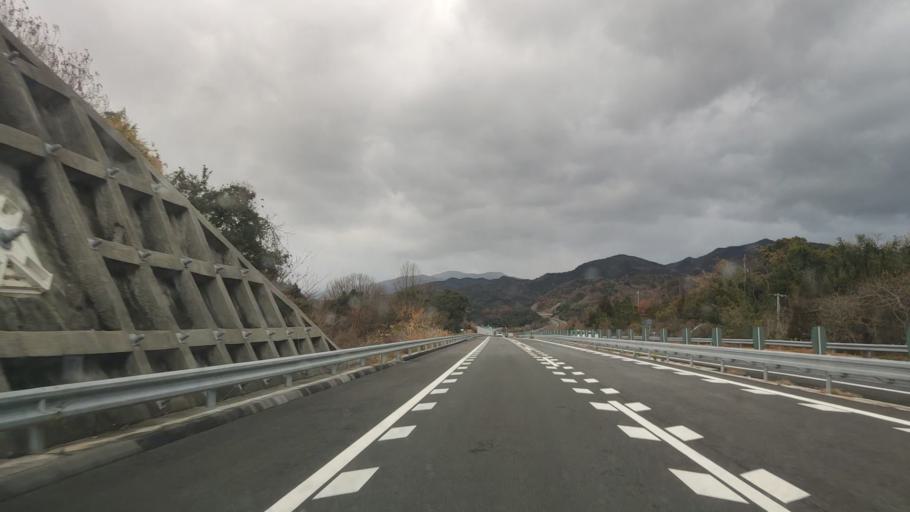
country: JP
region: Tokushima
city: Narutocho-mitsuishi
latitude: 34.1607
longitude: 134.5124
